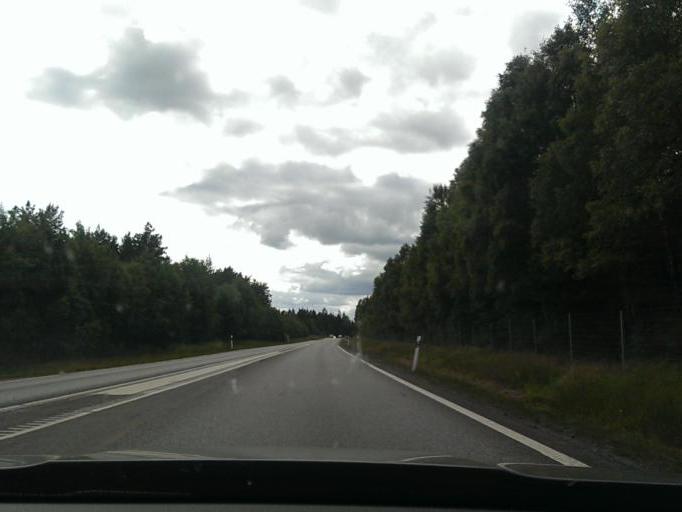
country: SE
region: Joenkoeping
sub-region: Varnamo Kommun
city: Forsheda
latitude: 57.1651
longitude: 13.8796
